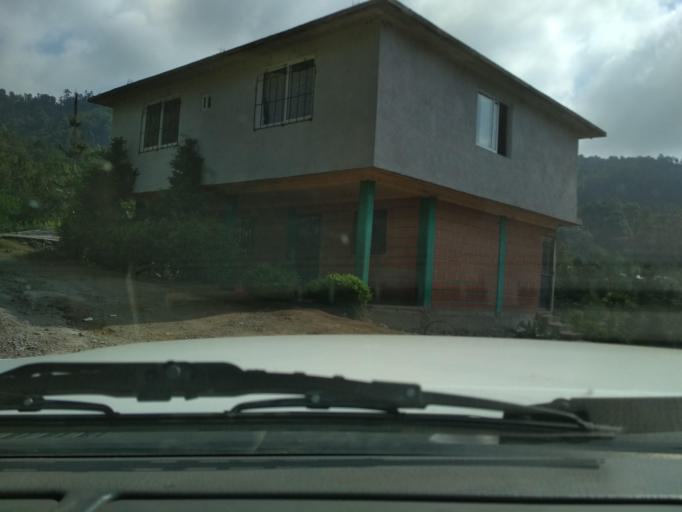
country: MX
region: Veracruz
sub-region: La Perla
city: Chilapa
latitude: 18.9942
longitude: -97.1795
